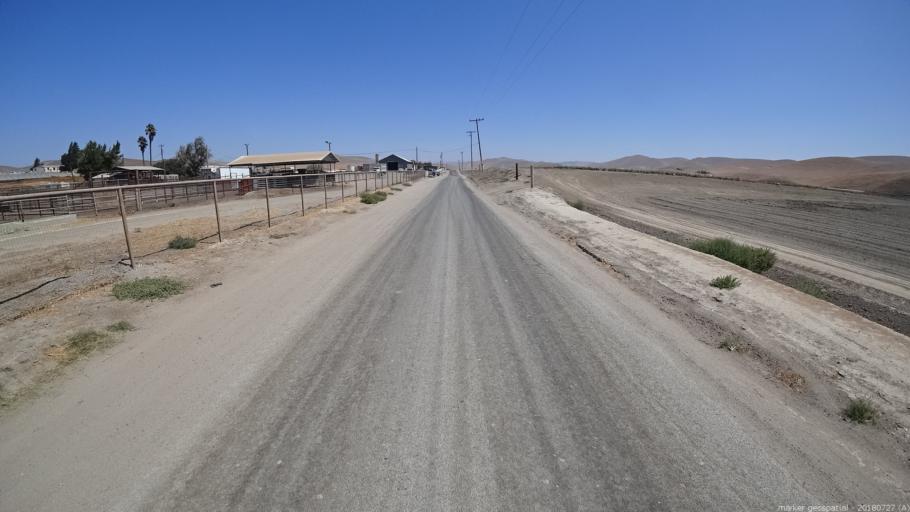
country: US
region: California
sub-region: Monterey County
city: King City
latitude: 36.0754
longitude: -120.9290
